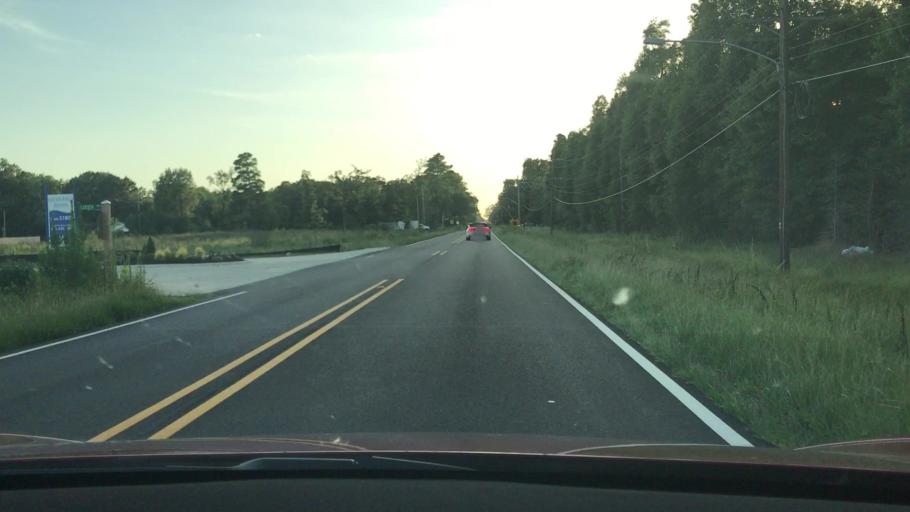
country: US
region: Louisiana
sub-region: Bossier Parish
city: Bossier City
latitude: 32.3909
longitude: -93.7362
